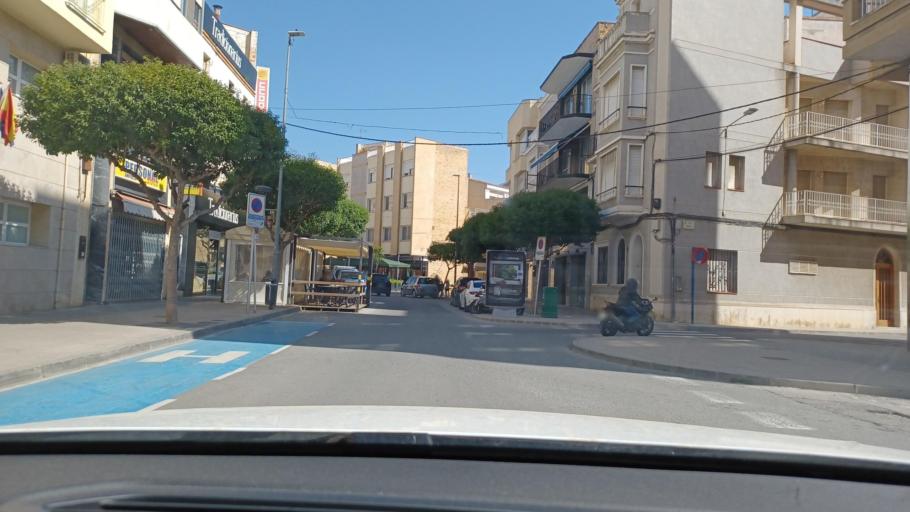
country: ES
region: Catalonia
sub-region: Provincia de Tarragona
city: Amposta
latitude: 40.7116
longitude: 0.5801
